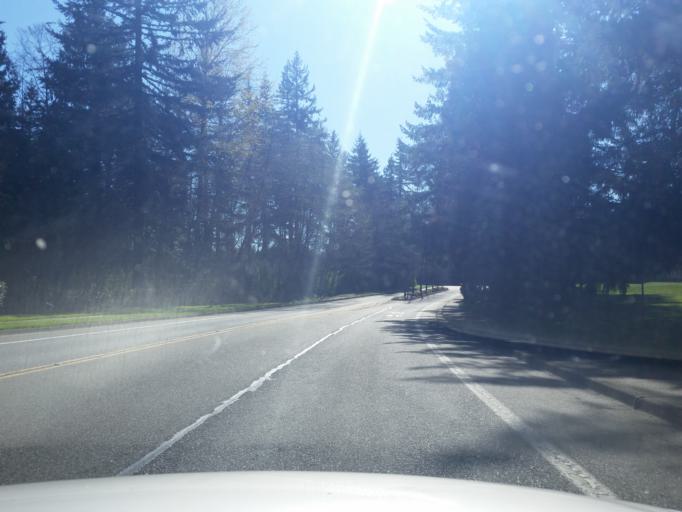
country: US
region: Washington
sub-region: Snohomish County
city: Mill Creek
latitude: 47.8525
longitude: -122.2002
